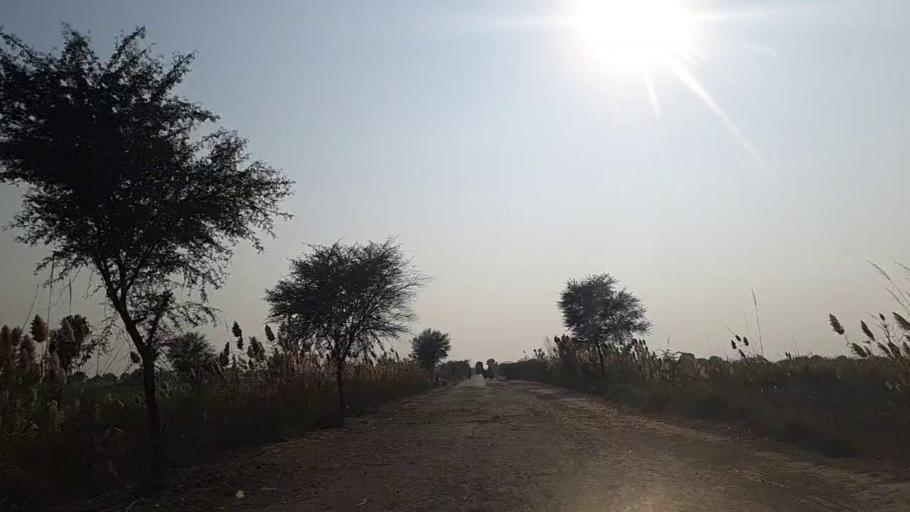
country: PK
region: Sindh
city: Jam Sahib
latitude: 26.2755
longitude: 68.6151
